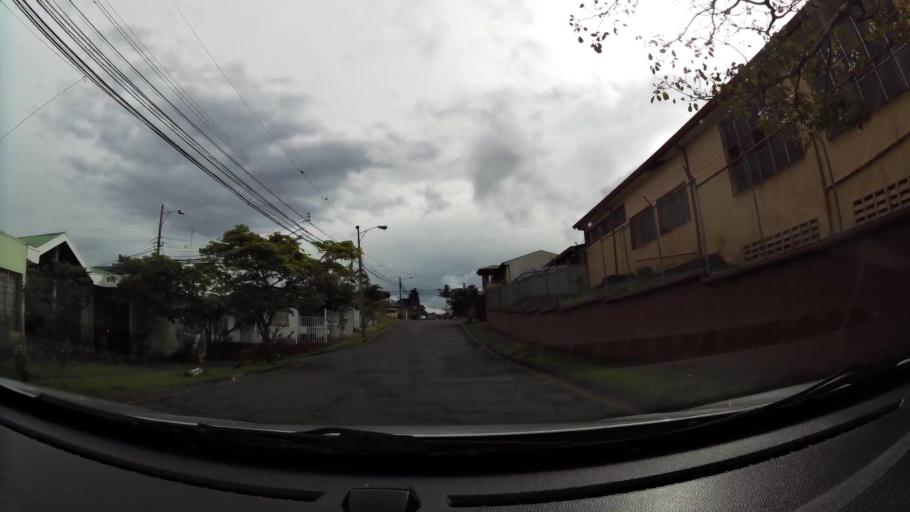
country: CR
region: San Jose
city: San Vicente de Moravia
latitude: 9.9583
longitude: -84.0565
